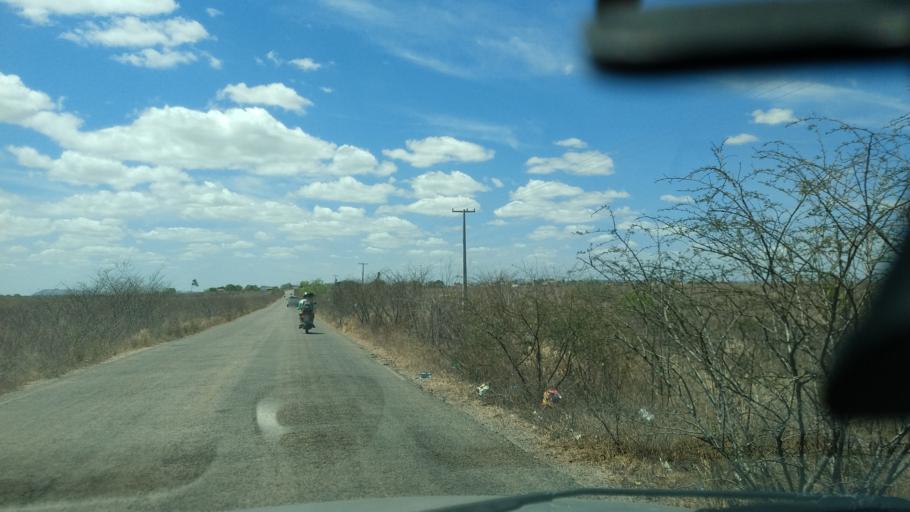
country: BR
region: Rio Grande do Norte
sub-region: Sao Paulo Do Potengi
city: Sao Paulo do Potengi
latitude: -5.9142
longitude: -35.7459
